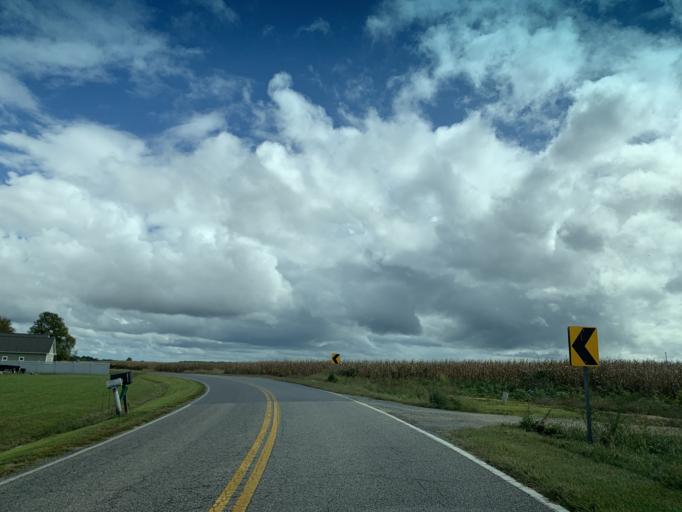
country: US
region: Maryland
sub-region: Caroline County
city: Denton
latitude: 38.9074
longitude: -75.8521
